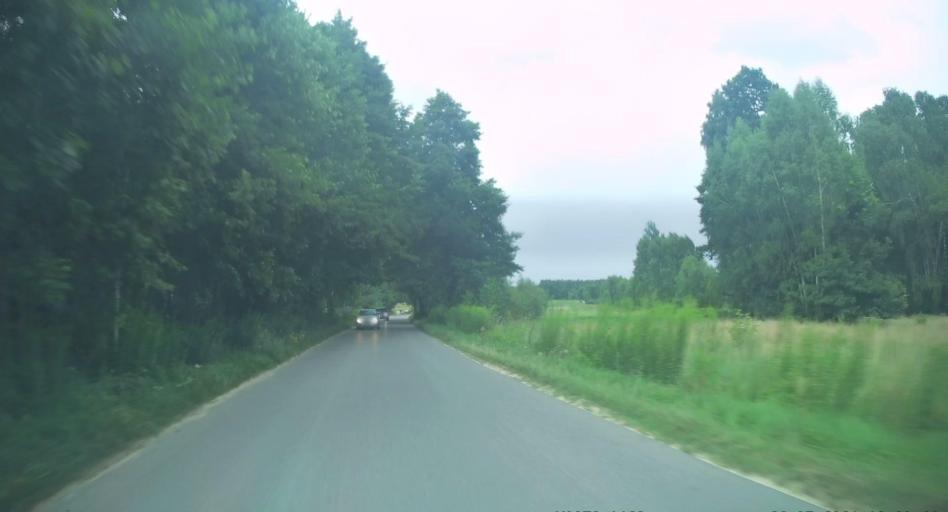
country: PL
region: Lodz Voivodeship
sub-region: Powiat rawski
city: Rawa Mazowiecka
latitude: 51.7417
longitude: 20.2007
